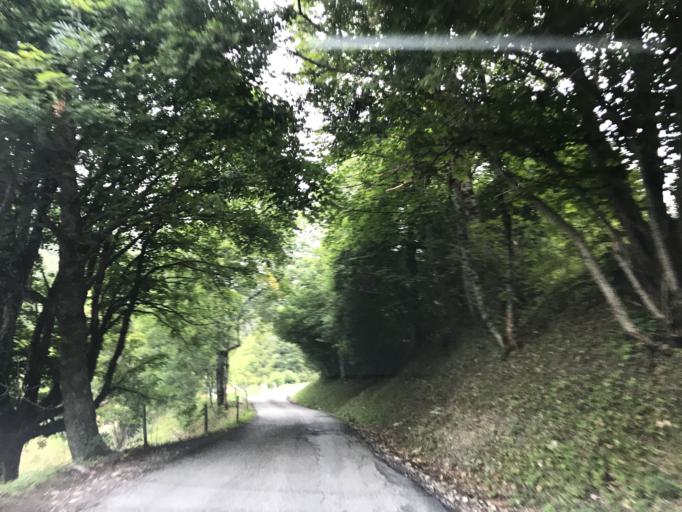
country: FR
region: Rhone-Alpes
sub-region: Departement de la Haute-Savoie
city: Talloires
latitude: 45.8175
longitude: 6.2615
